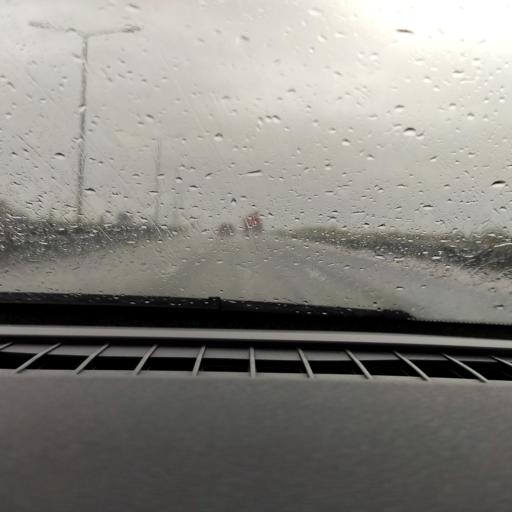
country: RU
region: Voronezj
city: Somovo
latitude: 51.7959
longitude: 39.2595
